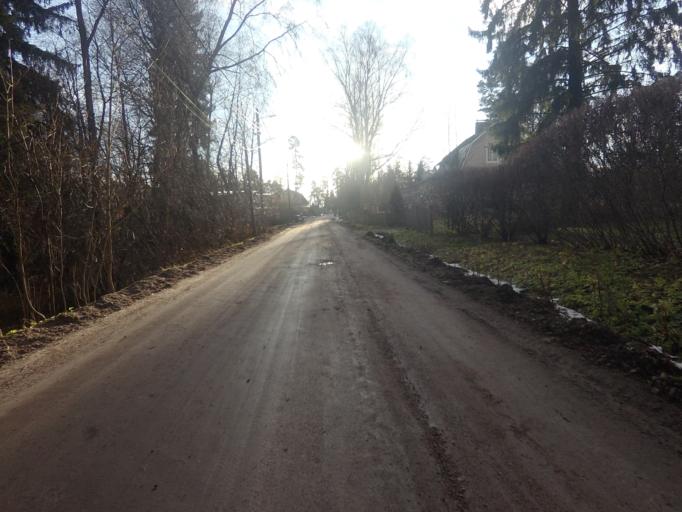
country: FI
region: Uusimaa
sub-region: Helsinki
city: Teekkarikylae
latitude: 60.2056
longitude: 24.8274
